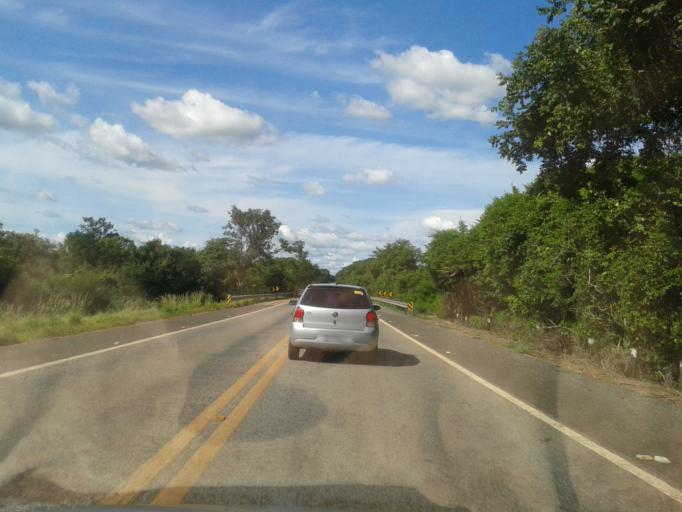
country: BR
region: Goias
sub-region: Mozarlandia
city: Mozarlandia
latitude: -15.0014
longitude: -50.5894
